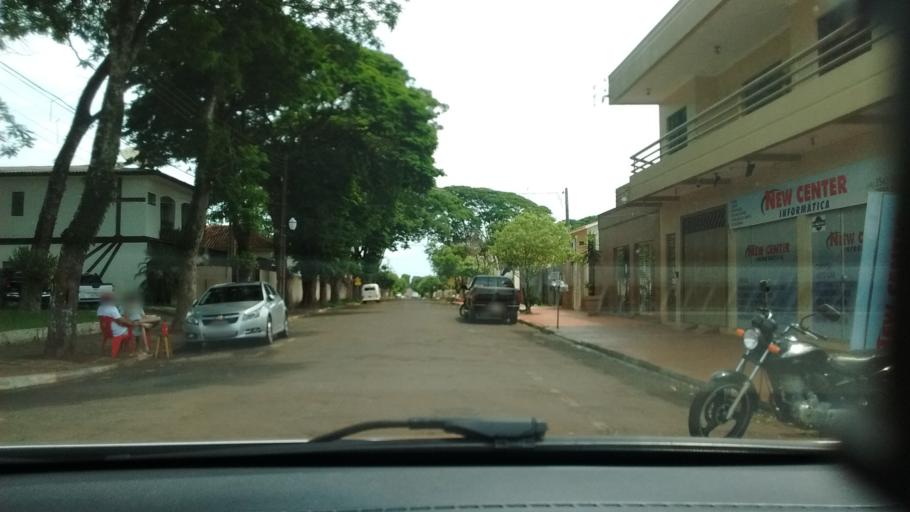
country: BR
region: Parana
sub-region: Corbelia
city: Corbelia
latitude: -24.5455
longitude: -52.9885
